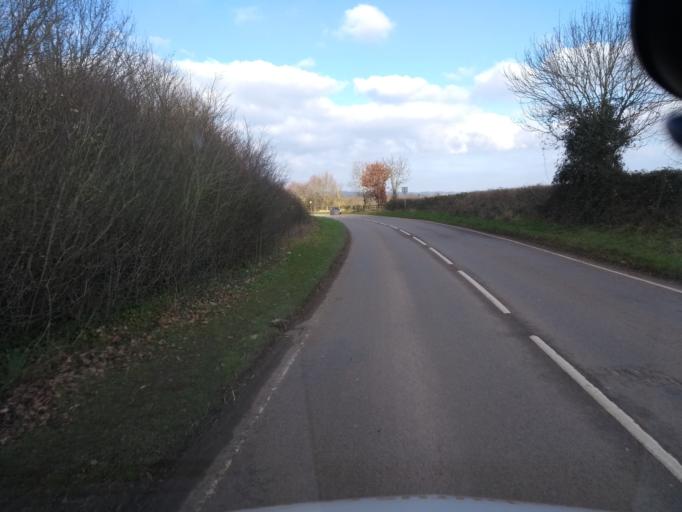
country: GB
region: England
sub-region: Somerset
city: Taunton
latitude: 50.9949
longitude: -3.0817
